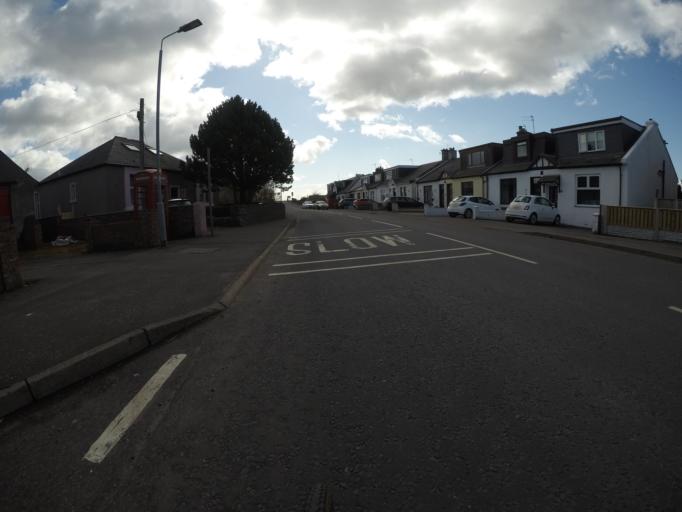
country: GB
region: Scotland
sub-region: North Ayrshire
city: Dreghorn
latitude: 55.5951
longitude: -4.6047
